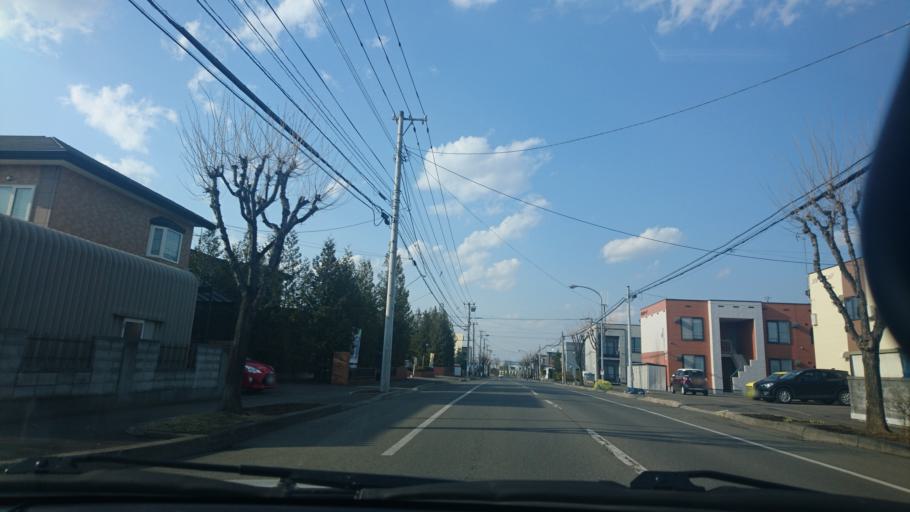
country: JP
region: Hokkaido
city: Obihiro
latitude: 42.9199
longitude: 143.1510
